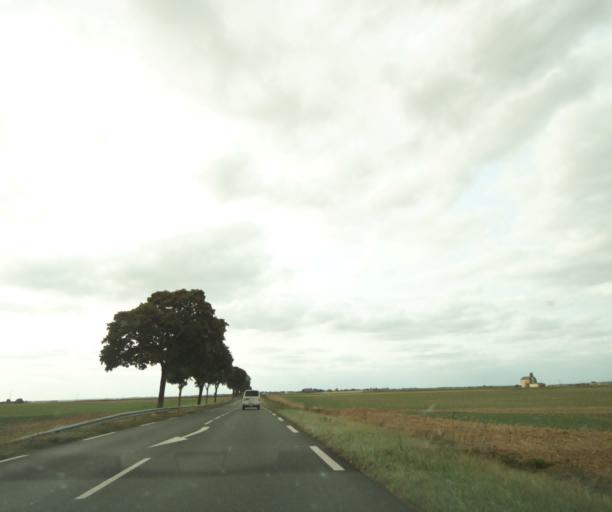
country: FR
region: Centre
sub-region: Departement d'Indre-et-Loire
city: Chambourg-sur-Indre
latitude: 47.1869
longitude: 0.9409
